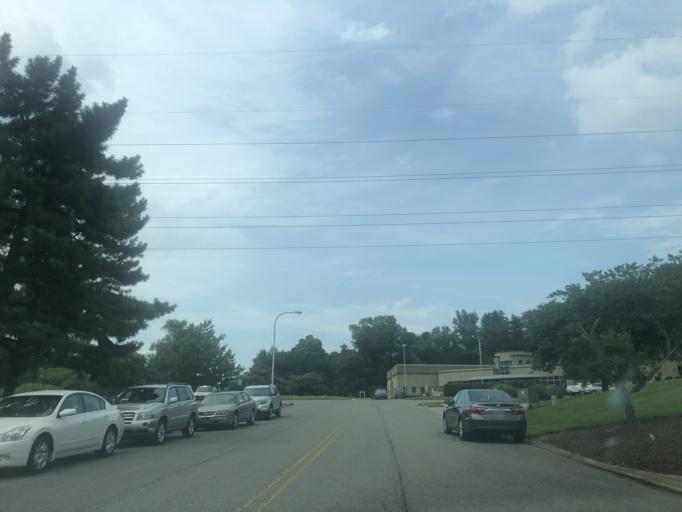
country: US
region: Tennessee
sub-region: Davidson County
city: Nashville
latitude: 36.1615
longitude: -86.6894
